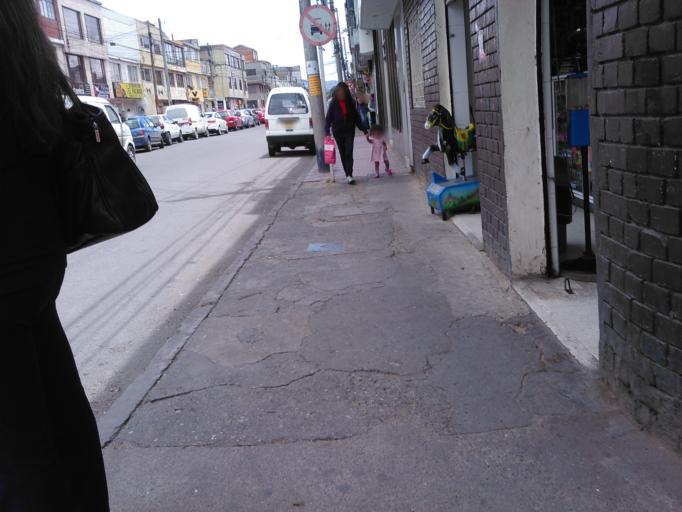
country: CO
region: Bogota D.C.
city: Bogota
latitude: 4.6242
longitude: -74.1158
